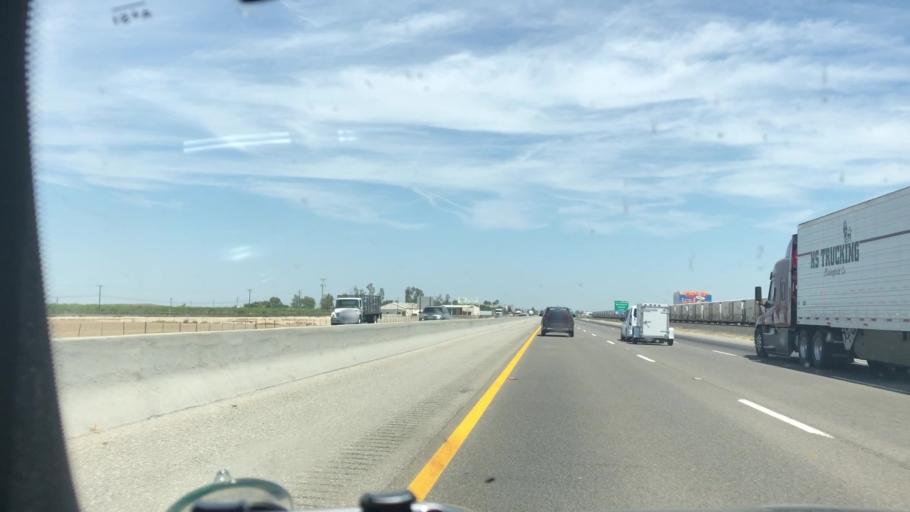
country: US
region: California
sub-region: Kern County
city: Delano
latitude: 35.7273
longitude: -119.2386
